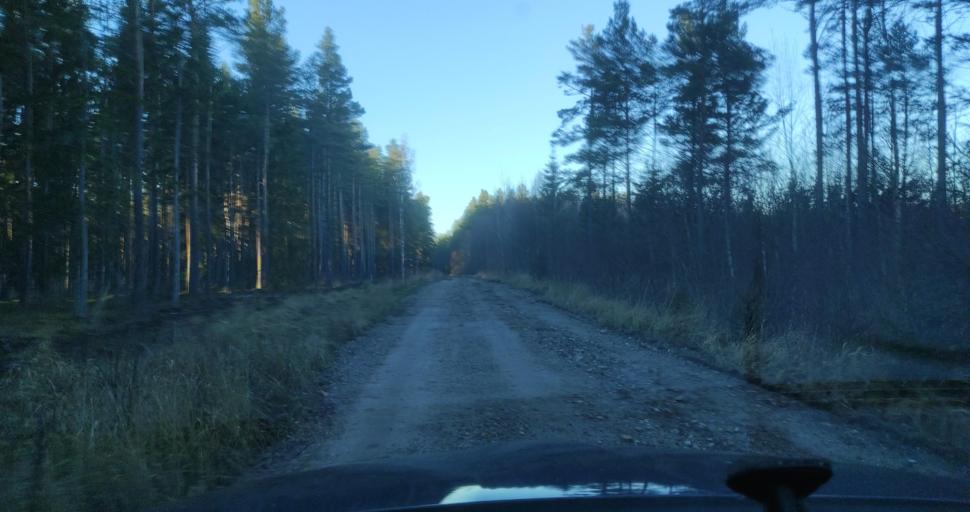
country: LV
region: Dundaga
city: Dundaga
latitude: 57.3808
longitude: 22.0816
